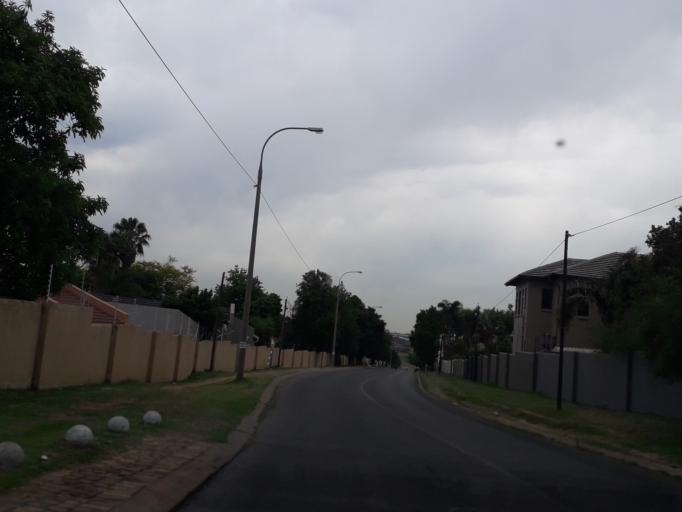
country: ZA
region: Gauteng
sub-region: City of Johannesburg Metropolitan Municipality
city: Roodepoort
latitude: -26.1020
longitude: 27.9242
